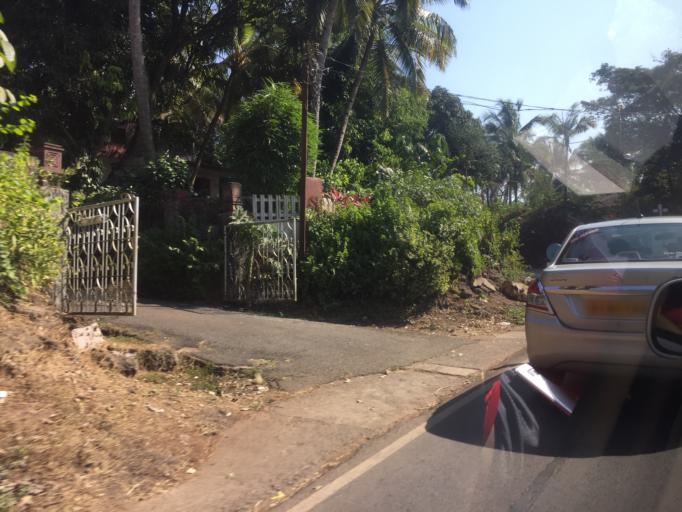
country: IN
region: Goa
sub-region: South Goa
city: Vasco Da Gama
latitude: 15.3945
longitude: 73.8183
